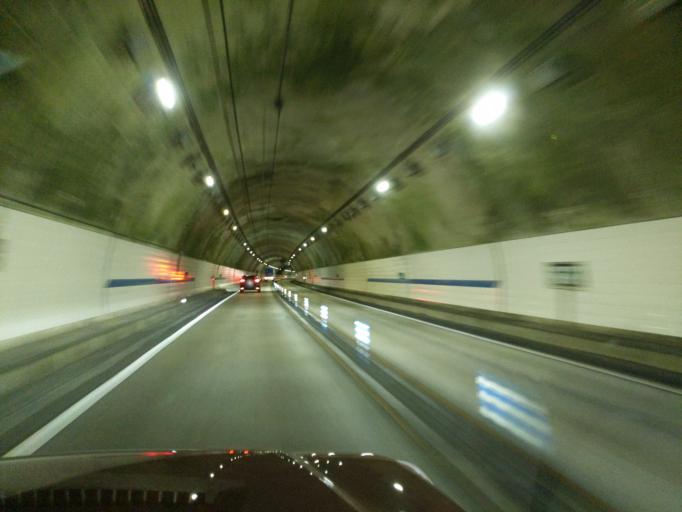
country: JP
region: Tokushima
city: Anan
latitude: 33.7919
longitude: 134.5923
